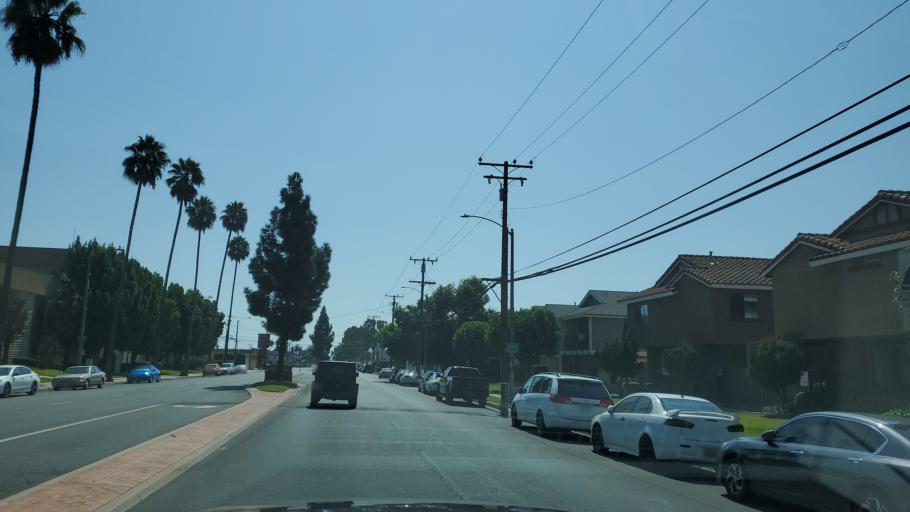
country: US
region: California
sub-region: Los Angeles County
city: Hawaiian Gardens
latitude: 33.8341
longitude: -118.0819
